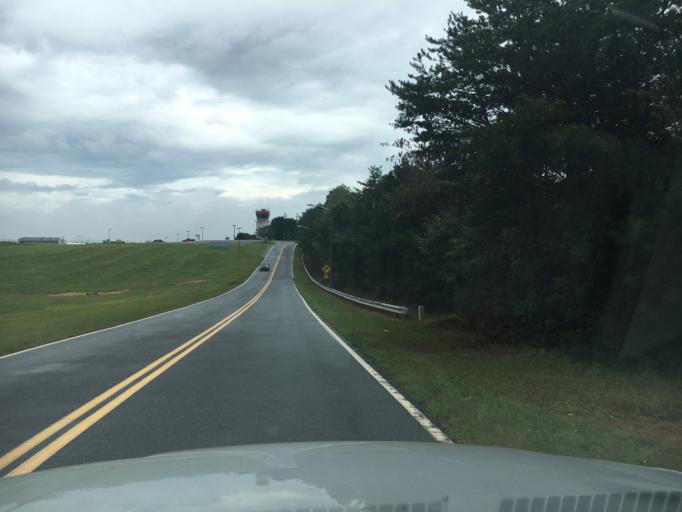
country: US
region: North Carolina
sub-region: Catawba County
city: Longview
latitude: 35.7439
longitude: -81.3851
